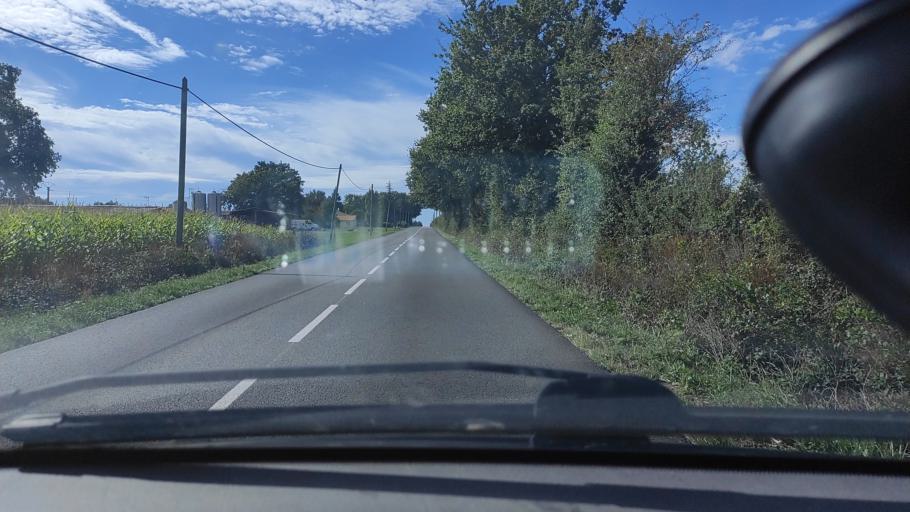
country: FR
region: Pays de la Loire
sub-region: Departement de la Vendee
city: La Boissiere-des-Landes
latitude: 46.5537
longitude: -1.4305
